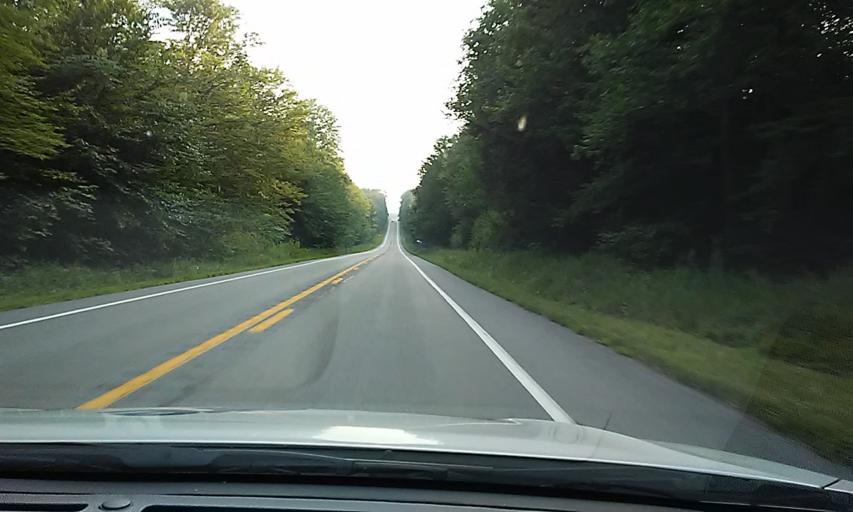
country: US
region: Pennsylvania
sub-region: Warren County
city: Sheffield
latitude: 41.5641
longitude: -78.9859
